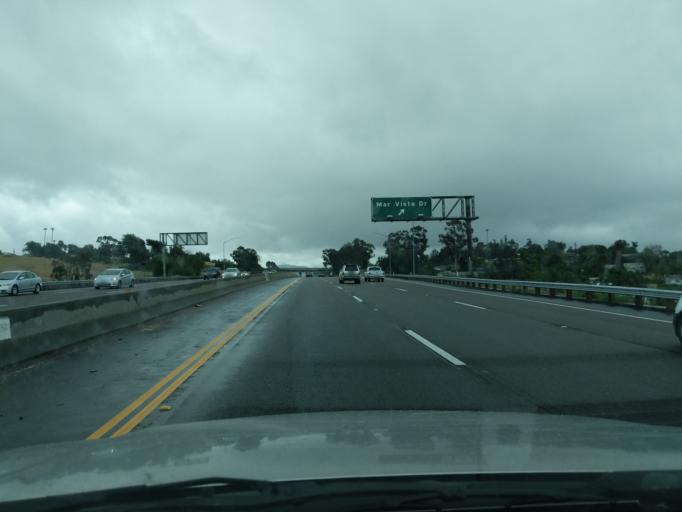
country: US
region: California
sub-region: San Diego County
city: Vista
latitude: 33.1840
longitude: -117.2324
